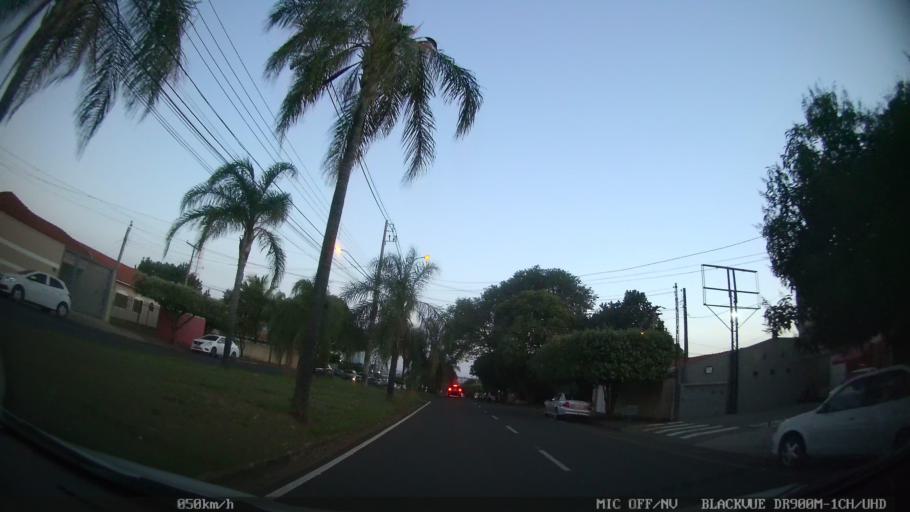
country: BR
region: Sao Paulo
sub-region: Sao Jose Do Rio Preto
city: Sao Jose do Rio Preto
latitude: -20.8047
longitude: -49.3484
